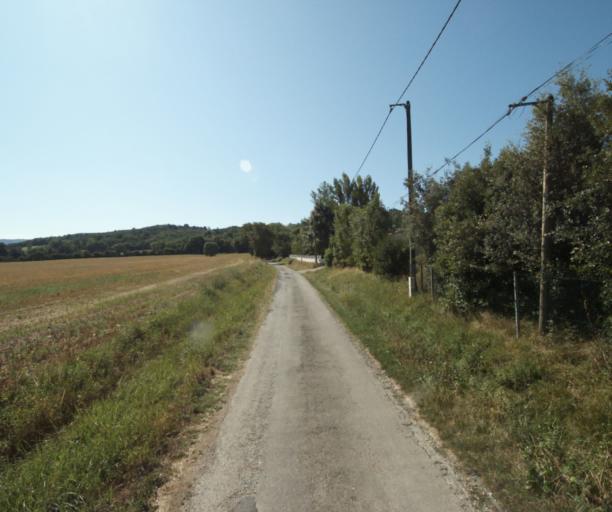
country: FR
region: Midi-Pyrenees
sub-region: Departement de la Haute-Garonne
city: Revel
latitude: 43.4501
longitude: 2.0191
